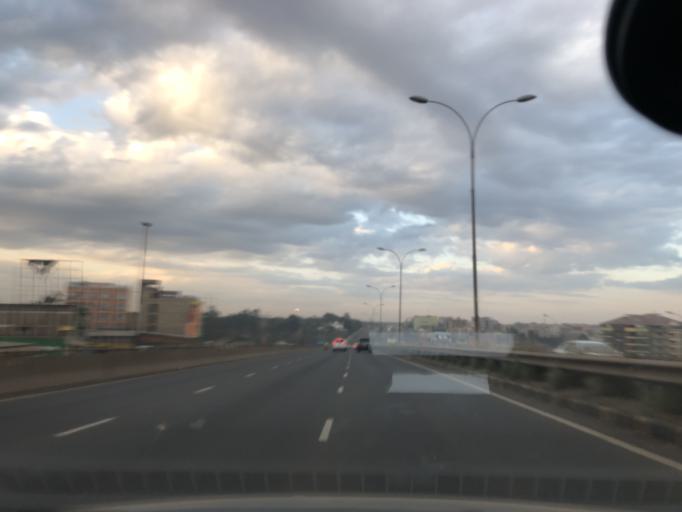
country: KE
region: Kiambu
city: Kiambu
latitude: -1.2035
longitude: 36.9171
